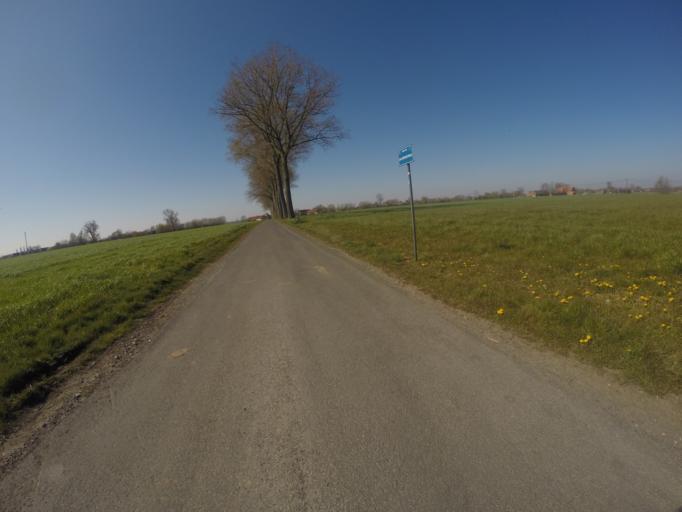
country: BE
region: Flanders
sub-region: Provincie West-Vlaanderen
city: Ruiselede
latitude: 51.0565
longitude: 3.4133
